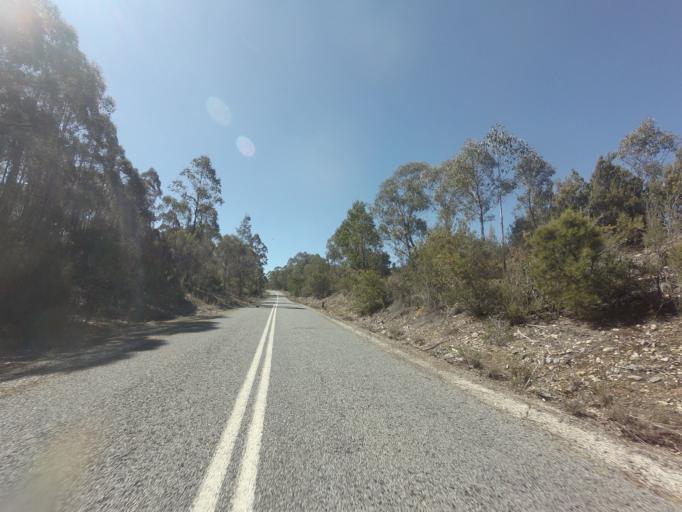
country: AU
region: Tasmania
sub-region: Huon Valley
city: Geeveston
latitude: -42.7750
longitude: 146.3974
